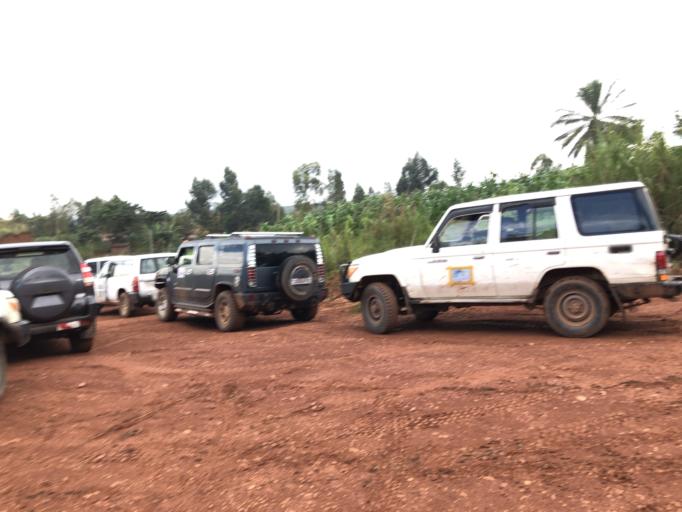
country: CD
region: Eastern Province
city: Bunia
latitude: 1.6974
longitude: 30.2828
